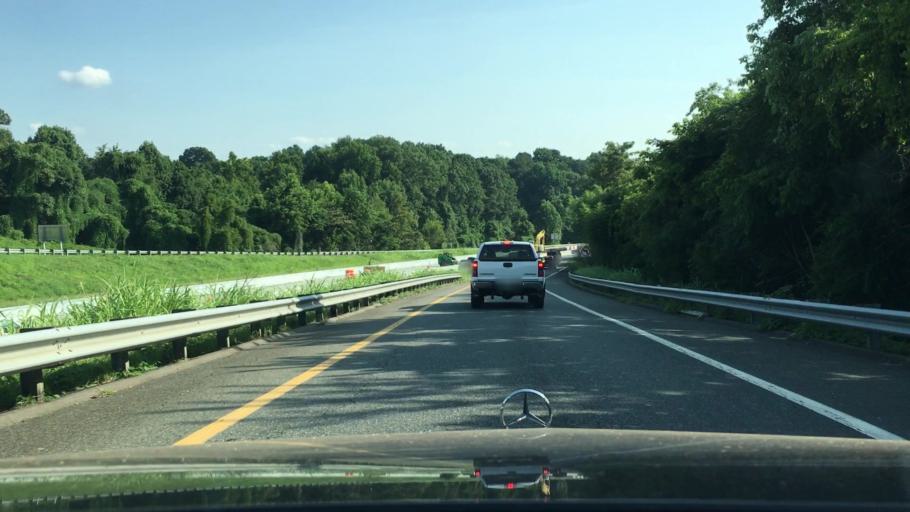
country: US
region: Virginia
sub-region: Amherst County
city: Madison Heights
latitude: 37.4211
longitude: -79.1237
